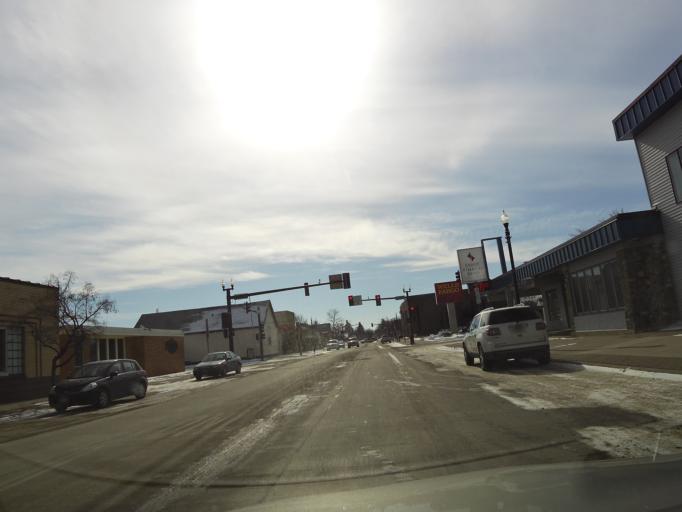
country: US
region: North Dakota
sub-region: Walsh County
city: Grafton
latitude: 48.4180
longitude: -97.4112
